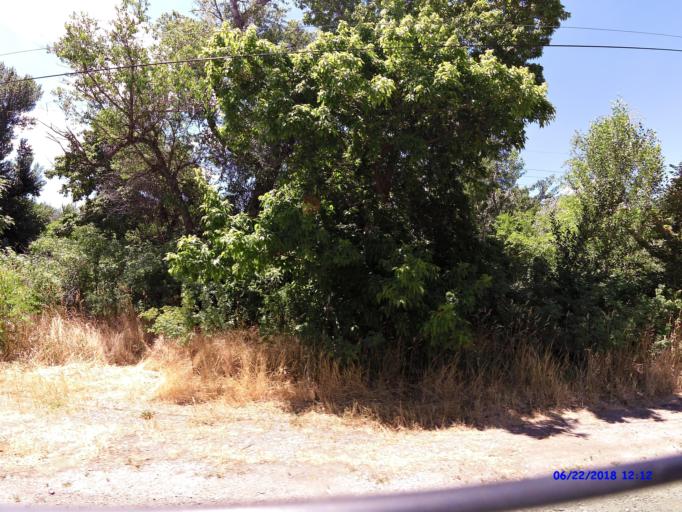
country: US
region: Utah
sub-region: Weber County
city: Ogden
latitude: 41.2363
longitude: -111.9567
